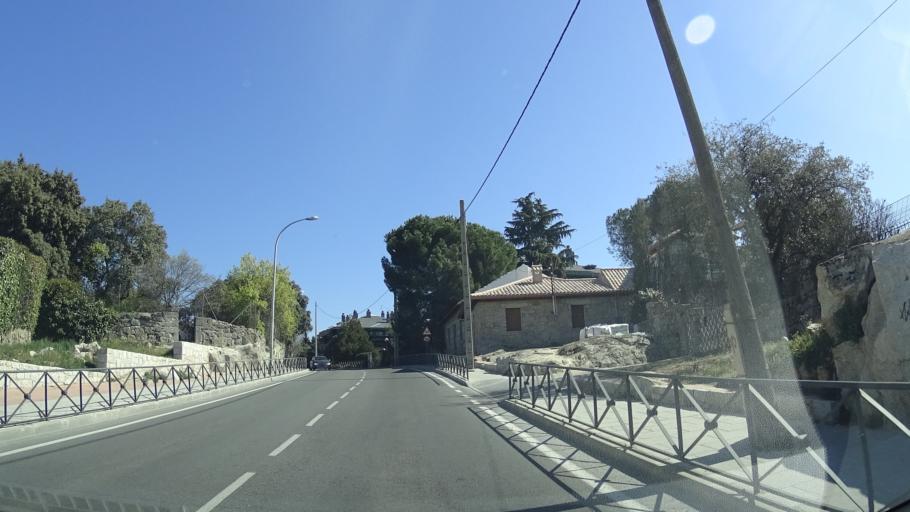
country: ES
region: Madrid
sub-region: Provincia de Madrid
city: Hoyo de Manzanares
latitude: 40.6223
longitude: -3.9032
